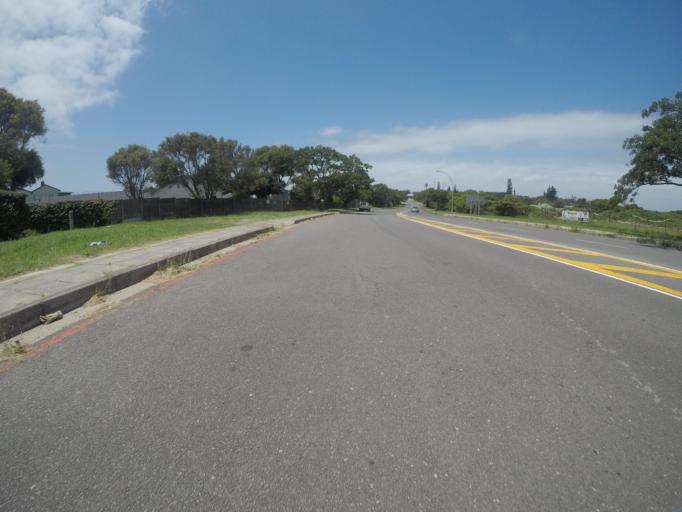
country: ZA
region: Eastern Cape
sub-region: Buffalo City Metropolitan Municipality
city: East London
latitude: -32.9936
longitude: 27.9210
